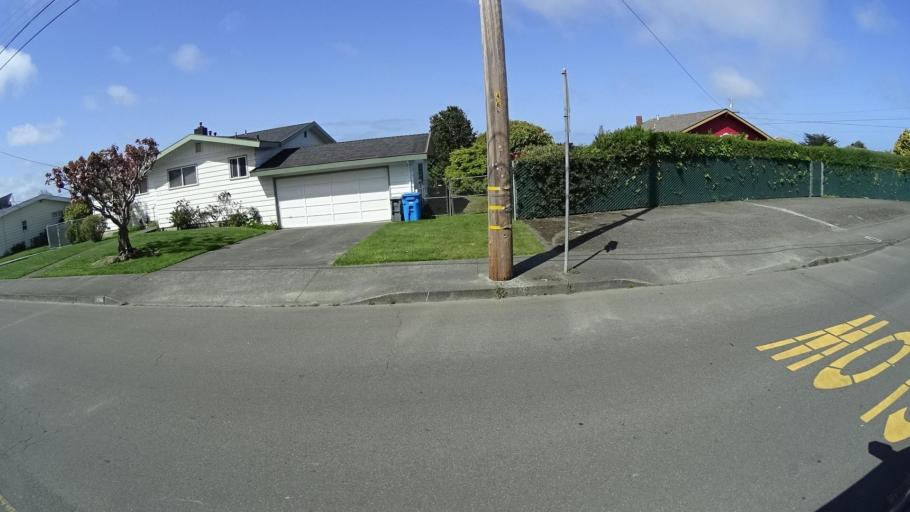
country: US
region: California
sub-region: Humboldt County
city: Bayview
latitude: 40.7765
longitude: -124.1800
